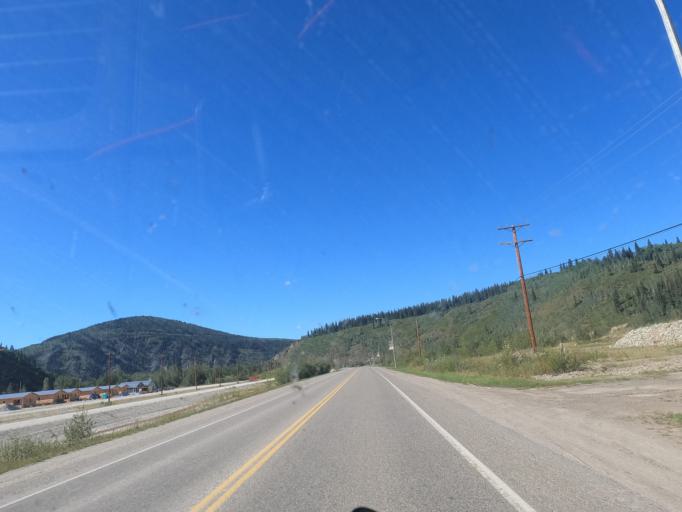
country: CA
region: Yukon
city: Dawson City
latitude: 64.0463
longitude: -139.4201
